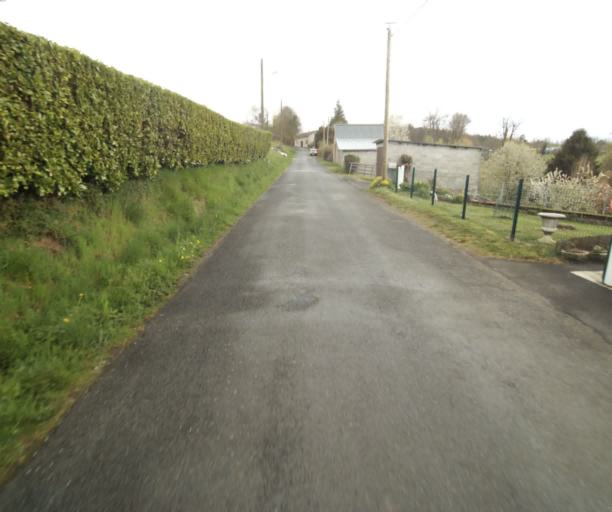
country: FR
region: Limousin
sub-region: Departement de la Correze
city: Tulle
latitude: 45.2762
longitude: 1.7482
